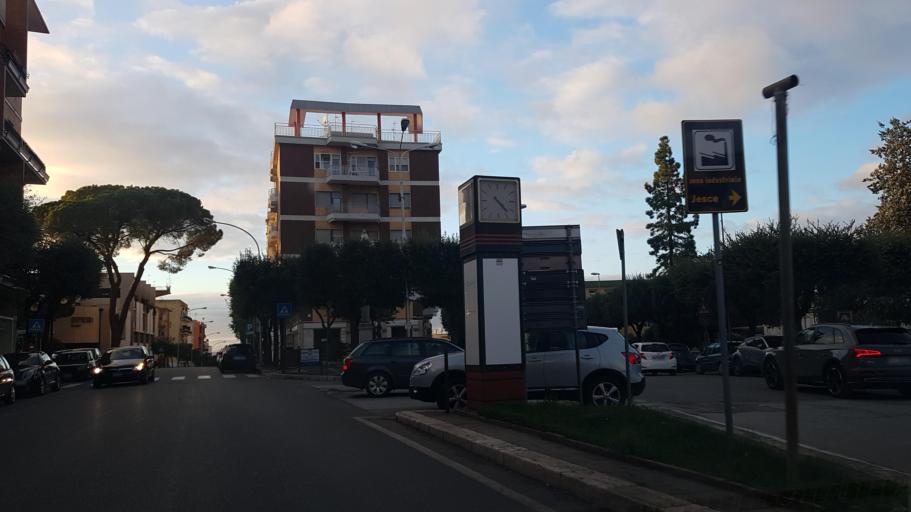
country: IT
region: Basilicate
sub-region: Provincia di Matera
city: Matera
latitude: 40.6724
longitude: 16.6026
